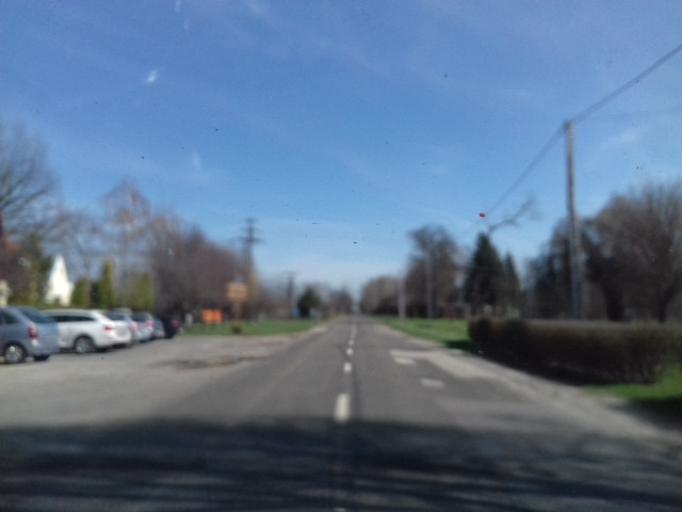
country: HU
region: Bacs-Kiskun
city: Kecskemet
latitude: 46.8933
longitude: 19.7339
